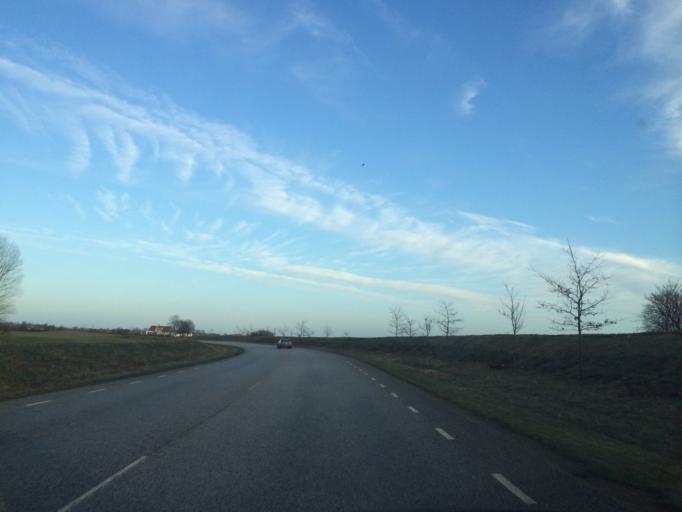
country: SE
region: Skane
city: Bjarred
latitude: 55.7281
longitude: 13.0364
